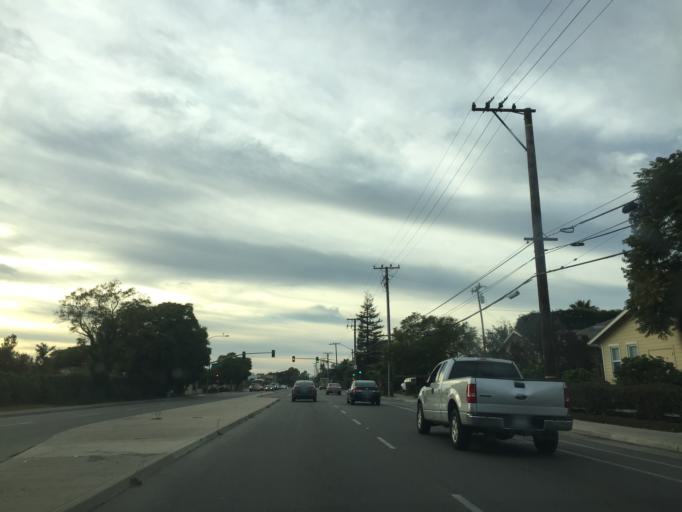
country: US
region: California
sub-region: Santa Barbara County
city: Goleta
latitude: 34.4349
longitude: -119.8046
